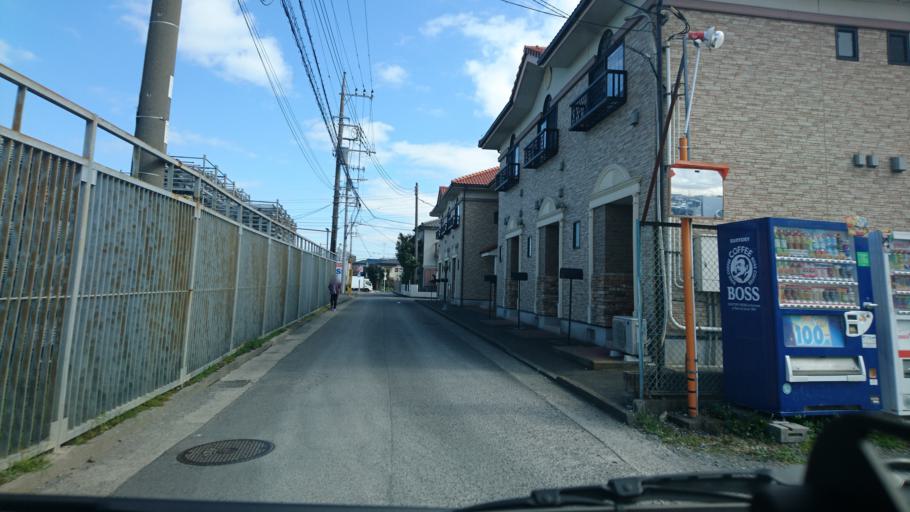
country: JP
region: Kanagawa
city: Zama
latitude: 35.5264
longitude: 139.3393
